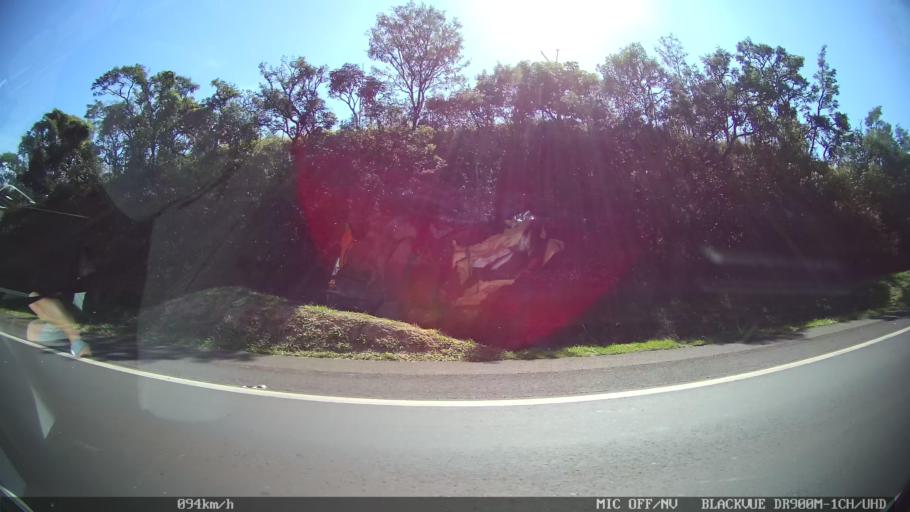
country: BR
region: Sao Paulo
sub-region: Franca
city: Franca
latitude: -20.5561
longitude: -47.4350
